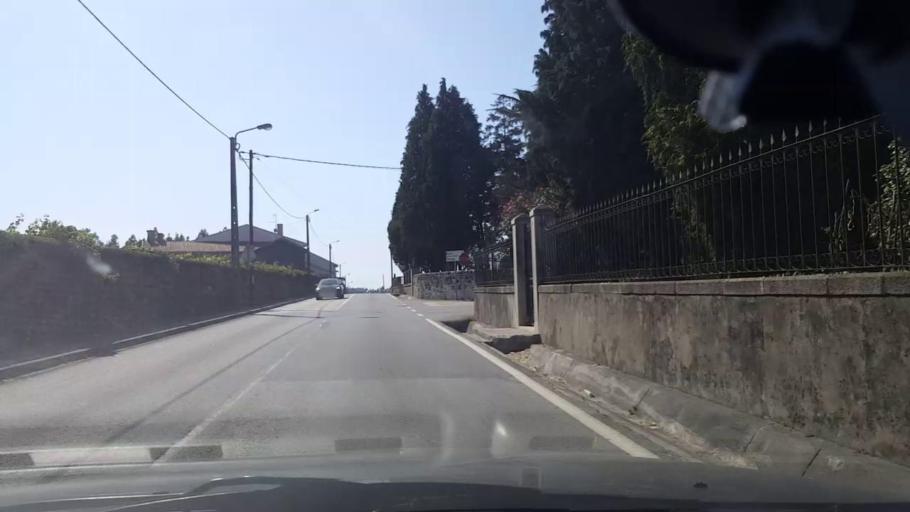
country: PT
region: Porto
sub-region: Povoa de Varzim
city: Pedroso
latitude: 41.3876
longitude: -8.7069
